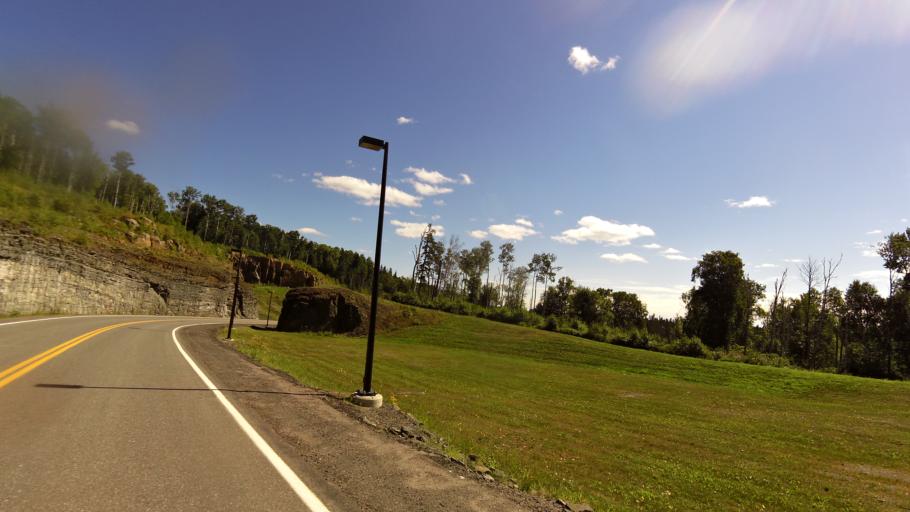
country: CA
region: Ontario
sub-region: Thunder Bay District
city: Thunder Bay
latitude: 48.4879
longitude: -89.1613
